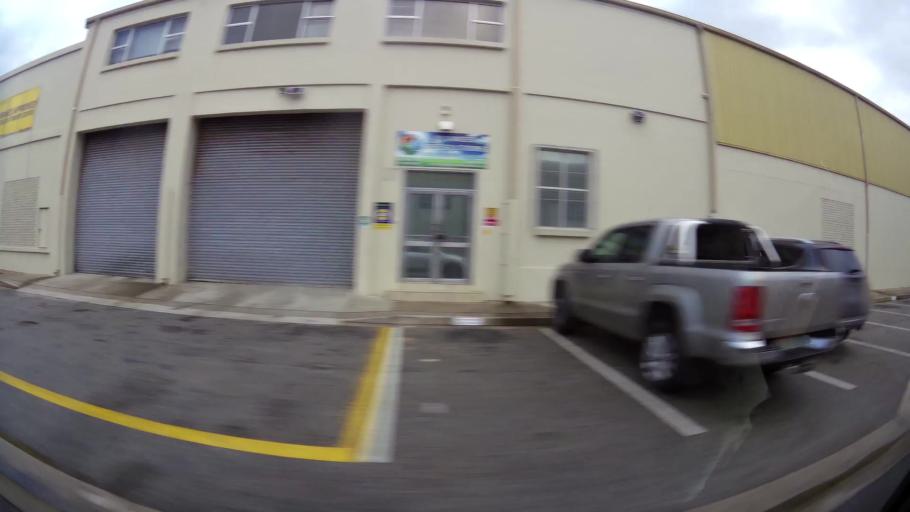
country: ZA
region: Eastern Cape
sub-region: Nelson Mandela Bay Metropolitan Municipality
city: Port Elizabeth
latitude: -33.9370
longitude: 25.6097
